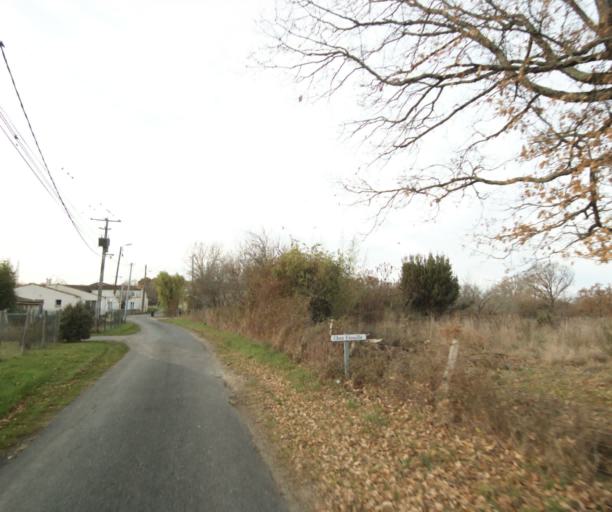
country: FR
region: Poitou-Charentes
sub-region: Departement de la Charente-Maritime
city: Fontcouverte
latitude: 45.7907
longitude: -0.5964
